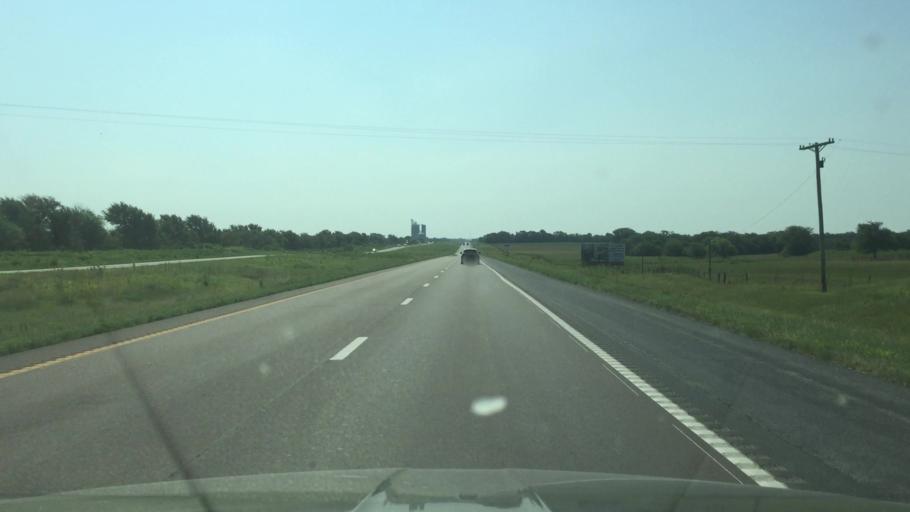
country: US
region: Missouri
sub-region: Pettis County
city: La Monte
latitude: 38.7598
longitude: -93.3730
